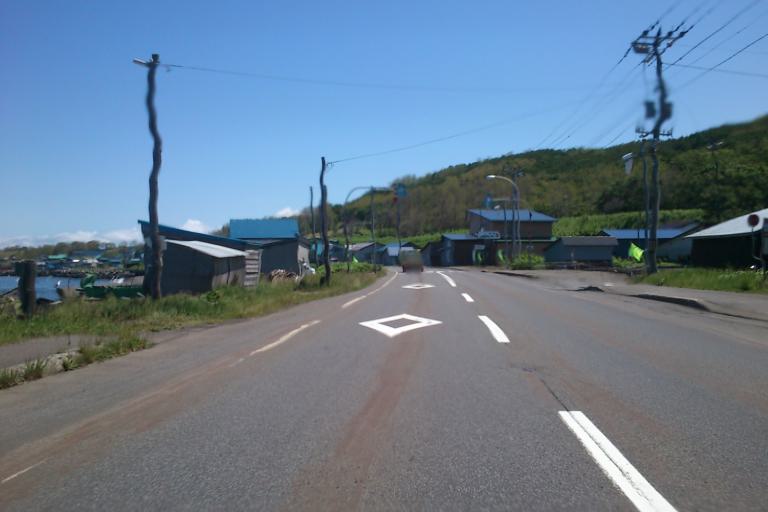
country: JP
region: Hokkaido
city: Rumoi
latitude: 43.8356
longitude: 141.4924
